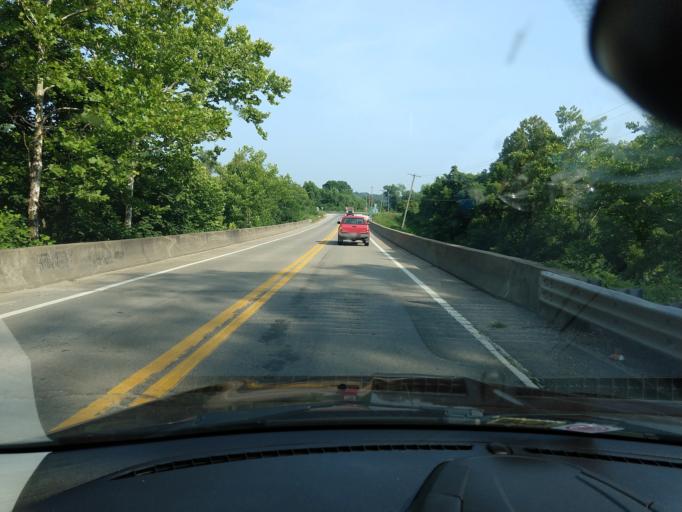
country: US
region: West Virginia
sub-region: Jackson County
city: Ravenswood
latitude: 38.8865
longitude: -81.8389
